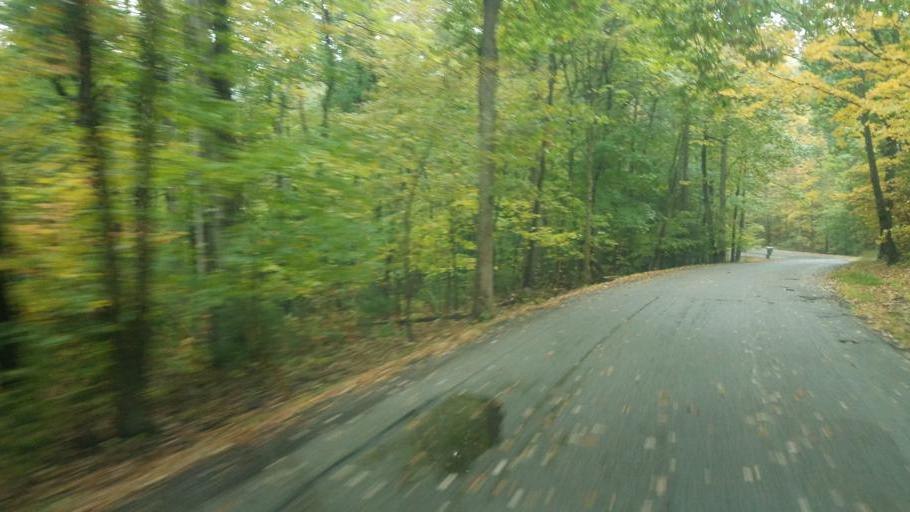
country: US
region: Ohio
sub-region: Ashland County
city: Loudonville
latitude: 40.6088
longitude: -82.2969
